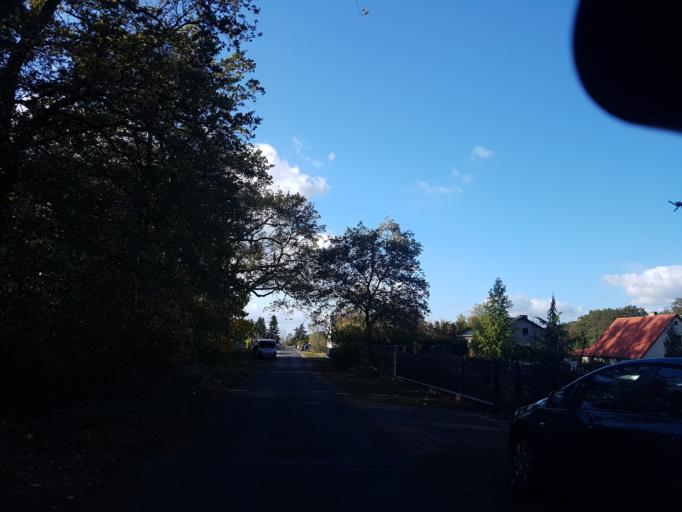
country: DE
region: Brandenburg
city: Nauen
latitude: 52.6357
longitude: 12.9053
